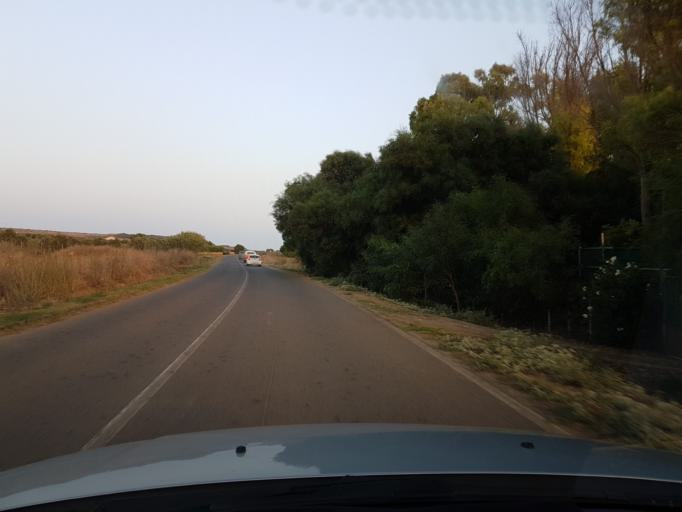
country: IT
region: Sardinia
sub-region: Provincia di Oristano
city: Cabras
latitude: 39.9465
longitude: 8.4318
